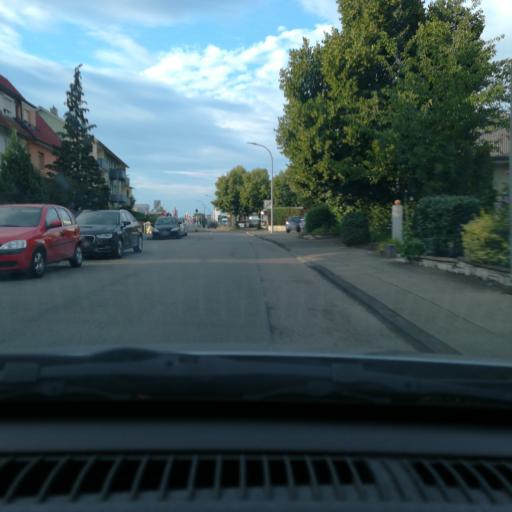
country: DE
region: Baden-Wuerttemberg
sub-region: Freiburg Region
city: Rielasingen-Worblingen
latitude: 47.7450
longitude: 8.8476
